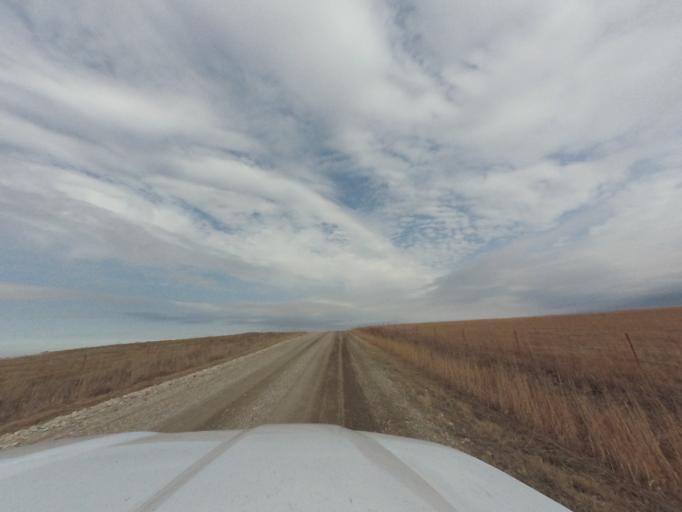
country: US
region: Kansas
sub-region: Chase County
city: Cottonwood Falls
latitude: 38.2294
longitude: -96.7306
